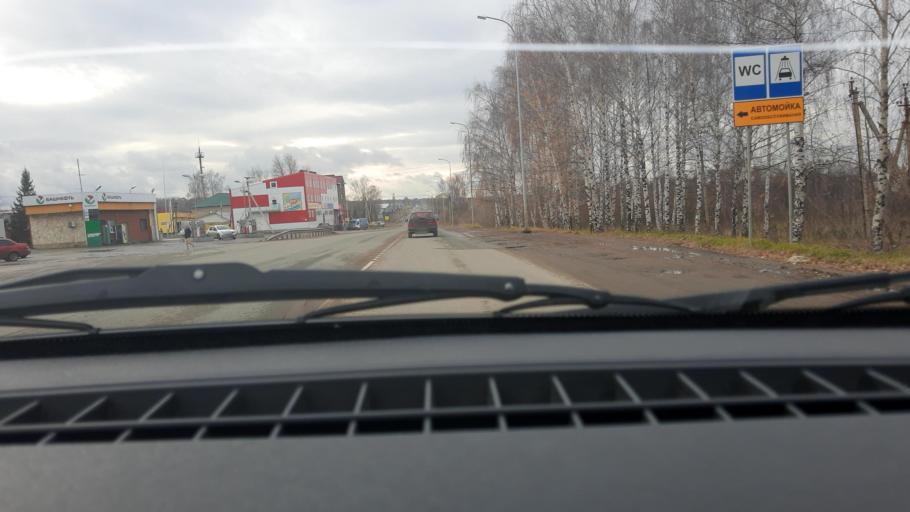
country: RU
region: Bashkortostan
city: Iglino
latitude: 54.8244
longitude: 56.3917
